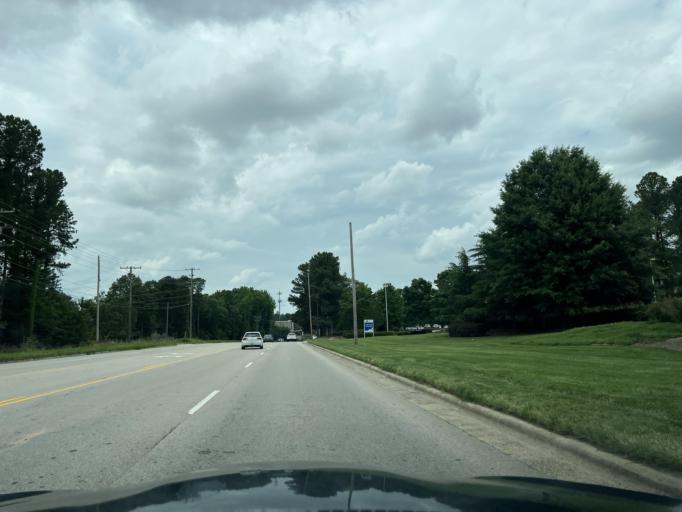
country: US
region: North Carolina
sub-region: Wake County
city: Morrisville
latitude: 35.8843
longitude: -78.8499
